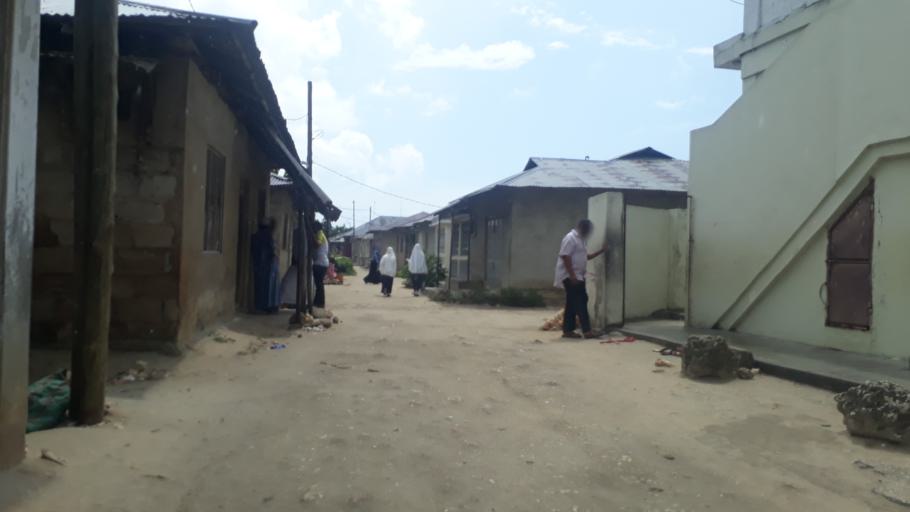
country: TZ
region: Zanzibar Urban/West
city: Zanzibar
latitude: -6.1788
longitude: 39.2098
